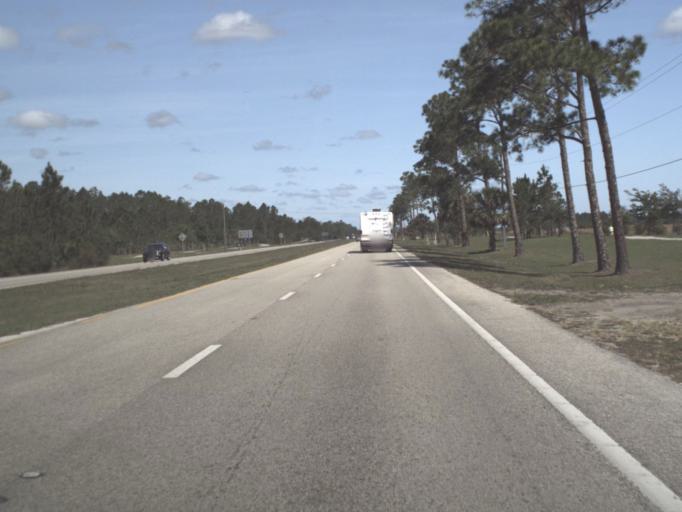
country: US
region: Florida
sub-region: Flagler County
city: Palm Coast
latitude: 29.5634
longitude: -81.2701
